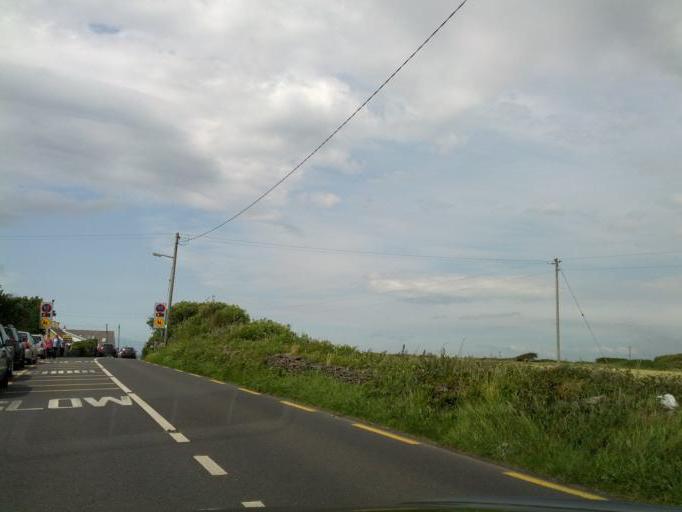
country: IE
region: Munster
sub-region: An Clar
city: Kilrush
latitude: 52.8092
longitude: -9.4536
